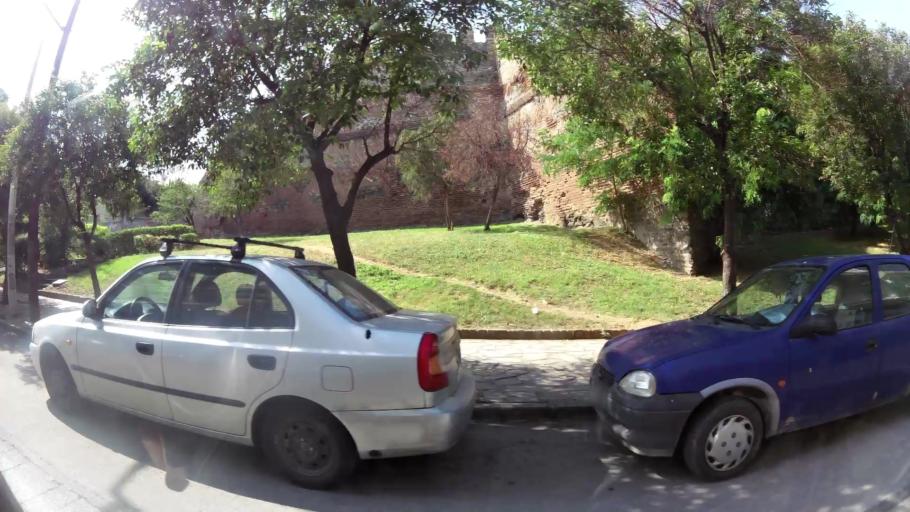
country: GR
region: Central Macedonia
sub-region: Nomos Thessalonikis
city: Thessaloniki
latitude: 40.6449
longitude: 22.9390
